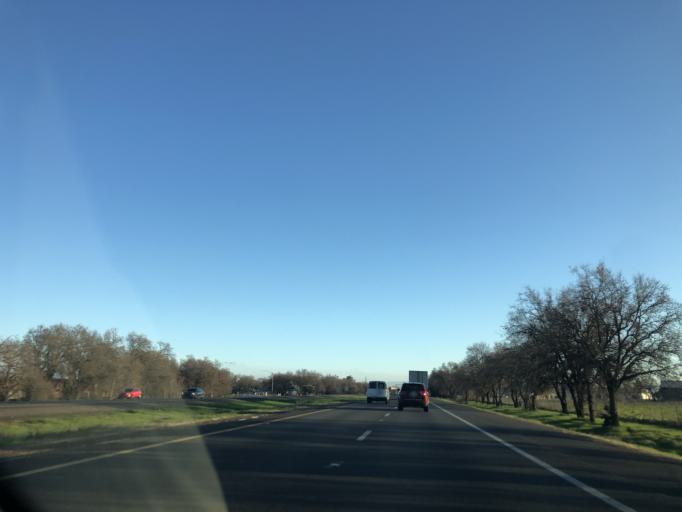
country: US
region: California
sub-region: Yolo County
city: Woodland
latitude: 38.6905
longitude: -121.7557
